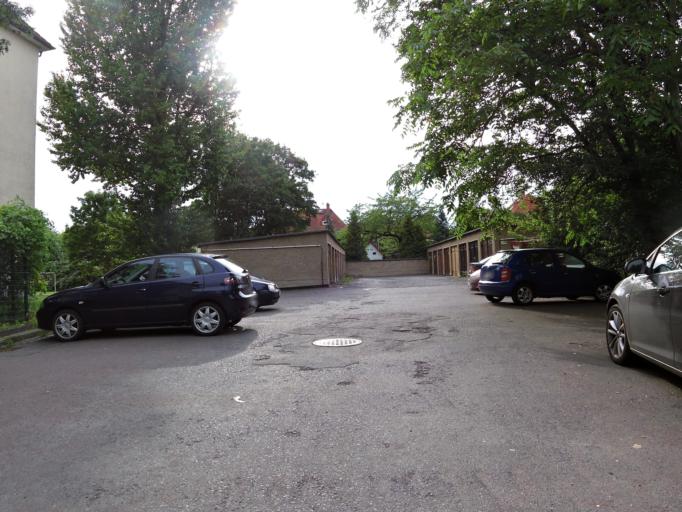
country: DE
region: Saxony
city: Leipzig
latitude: 51.3475
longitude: 12.4288
